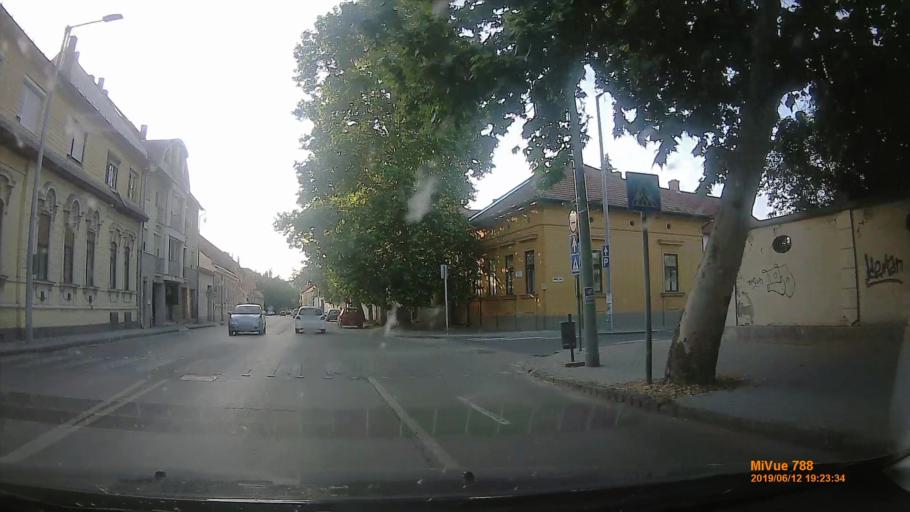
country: HU
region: Bacs-Kiskun
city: Kecskemet
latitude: 46.9112
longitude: 19.6914
